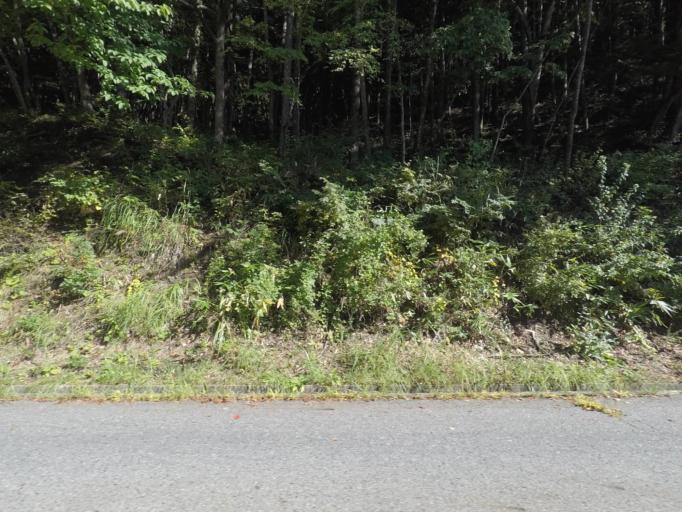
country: JP
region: Nagano
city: Tatsuno
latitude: 35.9738
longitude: 137.7629
